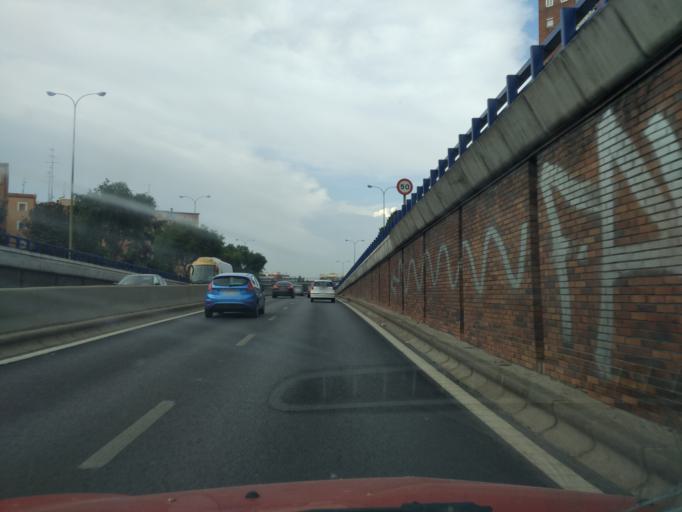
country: ES
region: Madrid
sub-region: Provincia de Madrid
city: Carabanchel
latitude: 40.3863
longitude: -3.7163
